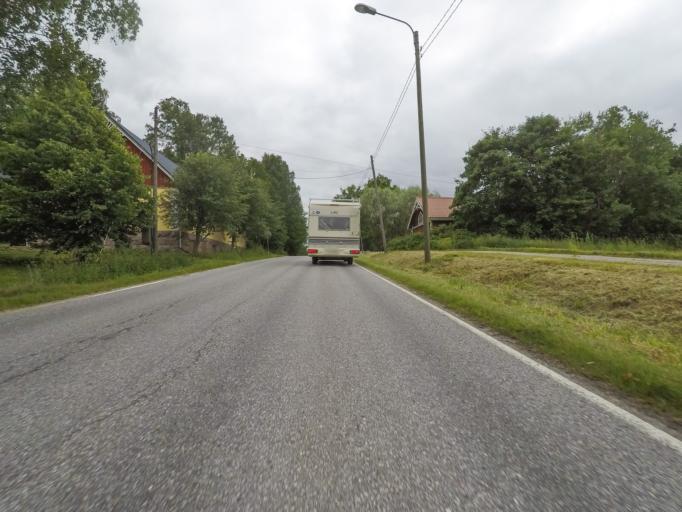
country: FI
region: Varsinais-Suomi
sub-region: Salo
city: Muurla
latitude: 60.3542
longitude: 23.2862
